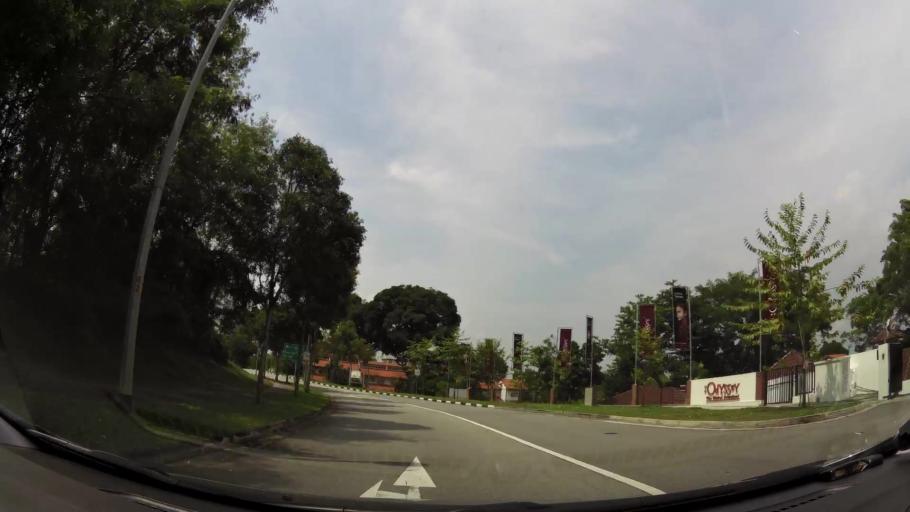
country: MY
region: Johor
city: Kampung Pasir Gudang Baru
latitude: 1.3795
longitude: 103.9627
